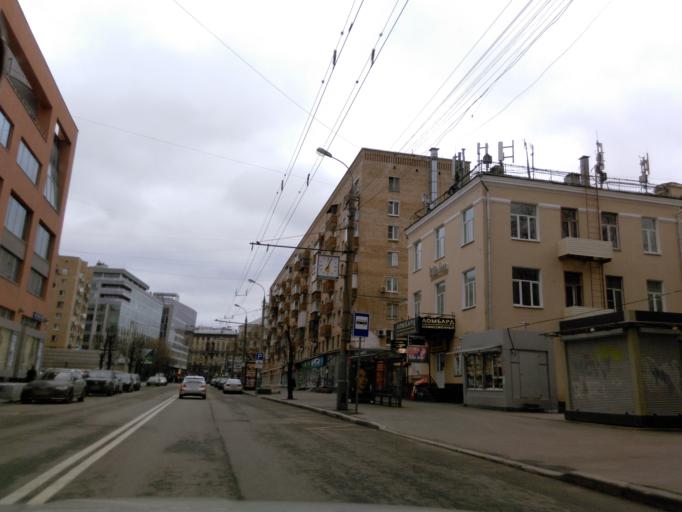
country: RU
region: Moskovskaya
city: Dorogomilovo
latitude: 55.7720
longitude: 37.5844
